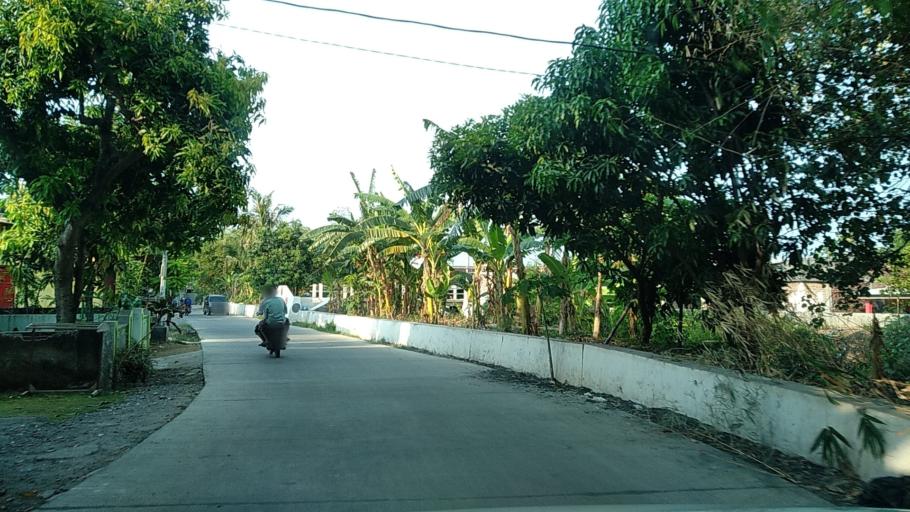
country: ID
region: Central Java
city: Semarang
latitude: -6.9608
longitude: 110.3025
